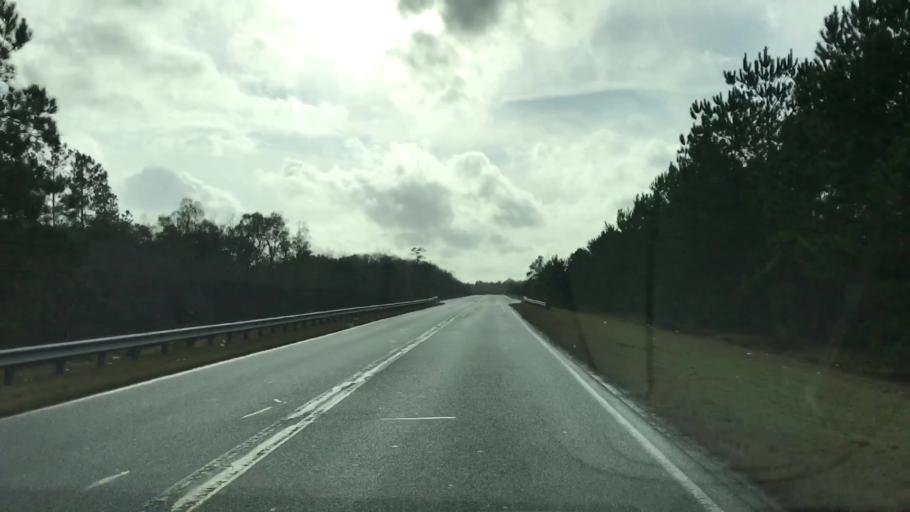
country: US
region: South Carolina
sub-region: Williamsburg County
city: Andrews
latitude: 33.4918
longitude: -79.5443
